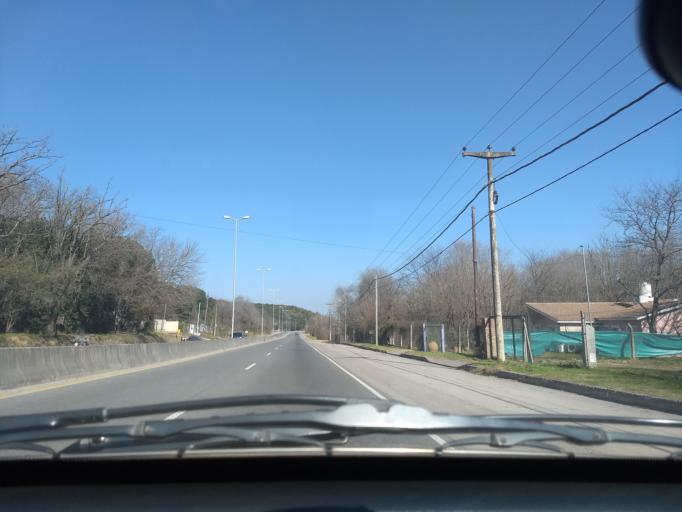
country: AR
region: Cordoba
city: Rio Ceballos
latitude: -31.1633
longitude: -64.3015
